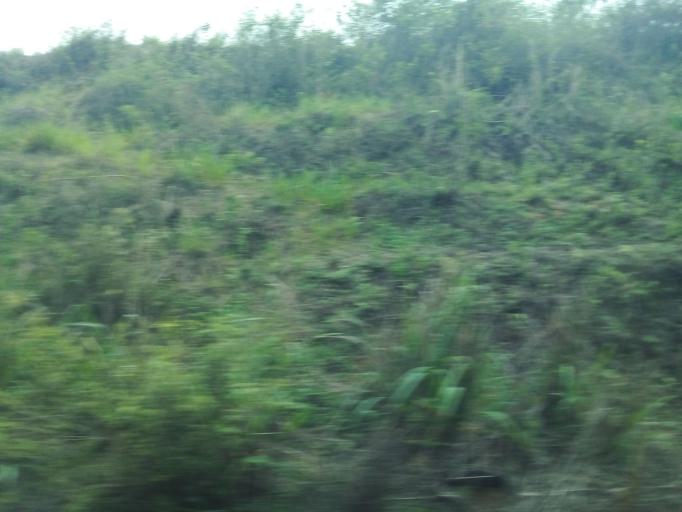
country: BR
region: Minas Gerais
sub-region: Ipatinga
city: Ipatinga
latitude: -19.4636
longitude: -42.4724
